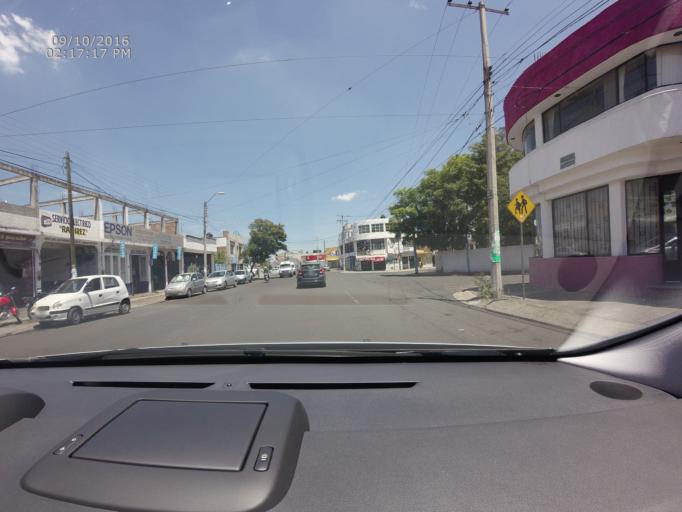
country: MX
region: Michoacan
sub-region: Morelia
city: Morelos
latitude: 19.6883
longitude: -101.2295
